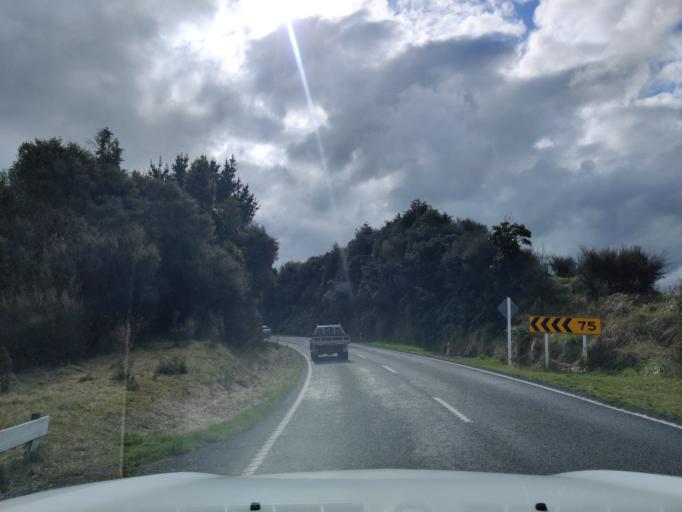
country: NZ
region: Manawatu-Wanganui
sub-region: Ruapehu District
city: Waiouru
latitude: -39.5059
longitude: 175.2950
